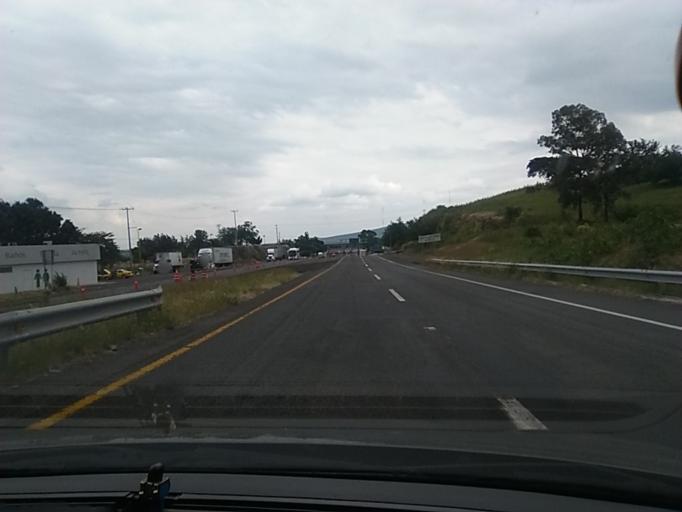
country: MX
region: Jalisco
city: Ocotlan
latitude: 20.4087
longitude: -102.7416
